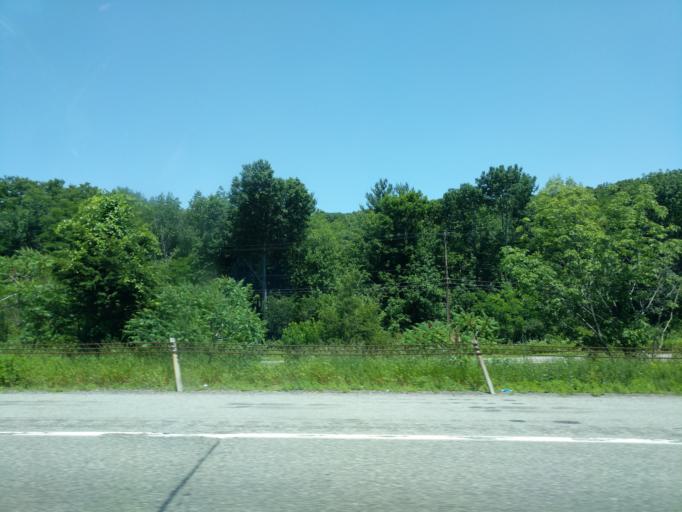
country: US
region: New York
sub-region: Orange County
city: Harriman
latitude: 41.3236
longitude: -74.1539
